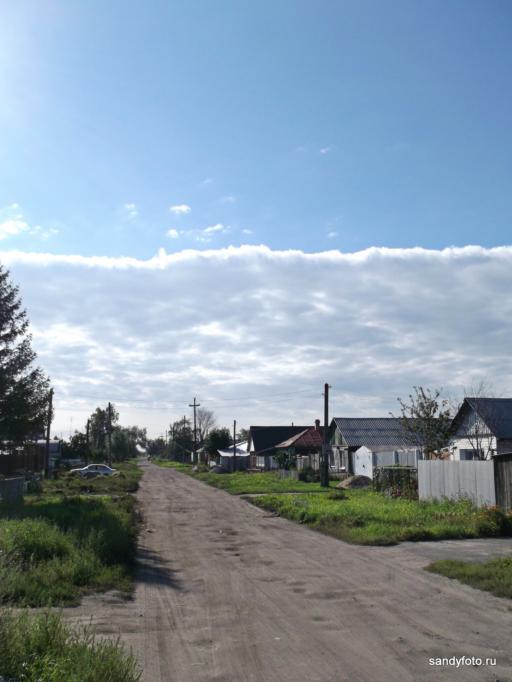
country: RU
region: Chelyabinsk
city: Troitsk
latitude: 54.1098
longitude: 61.5653
